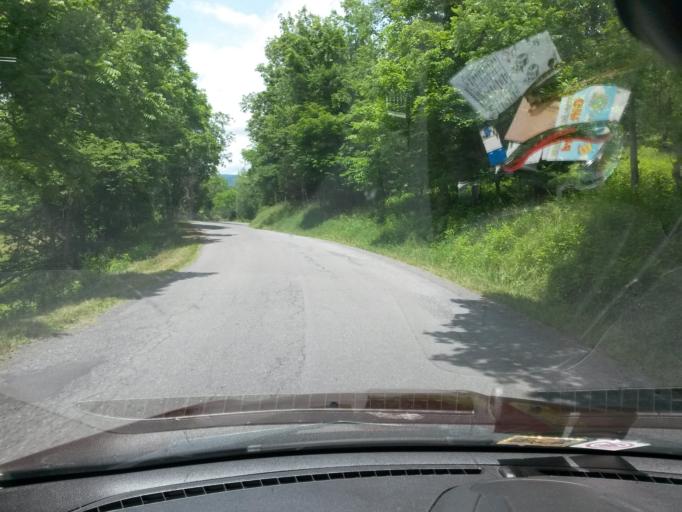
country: US
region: West Virginia
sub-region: Monroe County
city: Union
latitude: 37.5349
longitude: -80.5435
